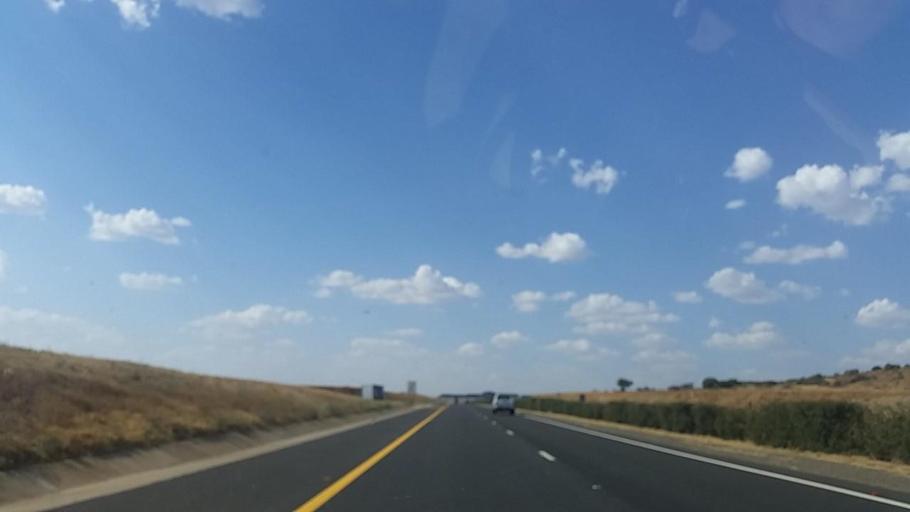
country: ZA
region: Orange Free State
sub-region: Mangaung Metropolitan Municipality
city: Bloemfontein
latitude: -29.2010
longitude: 26.1908
